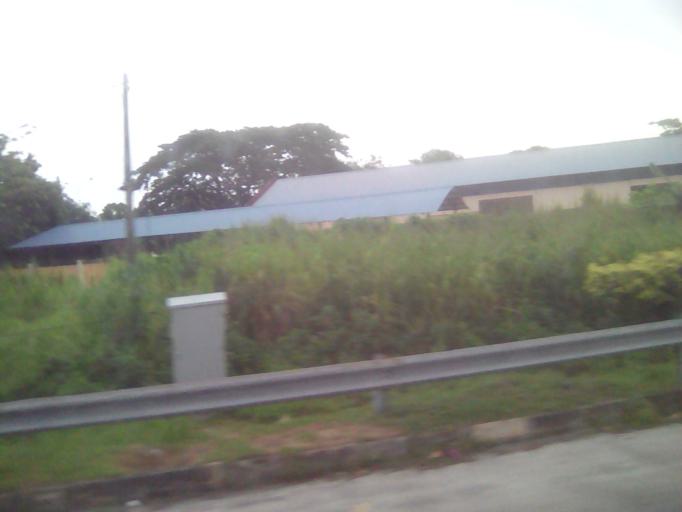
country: MY
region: Penang
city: Butterworth
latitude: 5.4056
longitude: 100.3767
